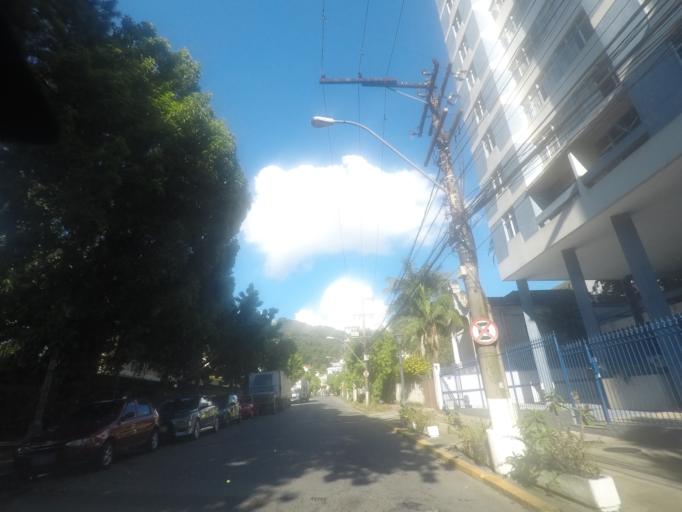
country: BR
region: Rio de Janeiro
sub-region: Petropolis
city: Petropolis
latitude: -22.5082
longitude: -43.1683
